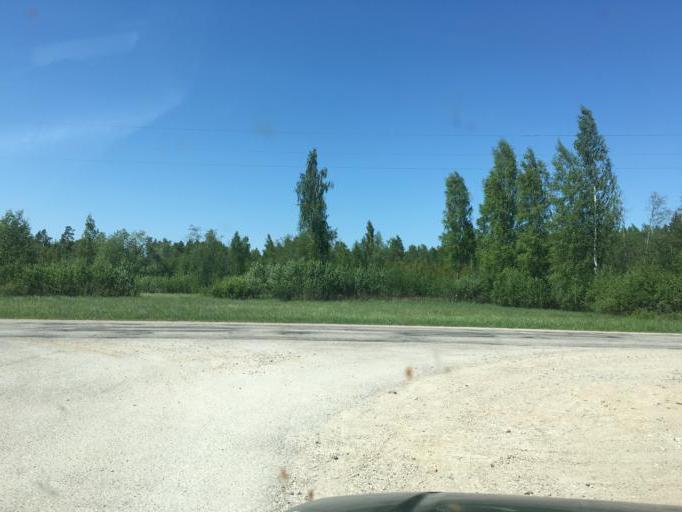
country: LV
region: Talsu Rajons
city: Valdemarpils
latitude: 57.4498
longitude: 22.6548
